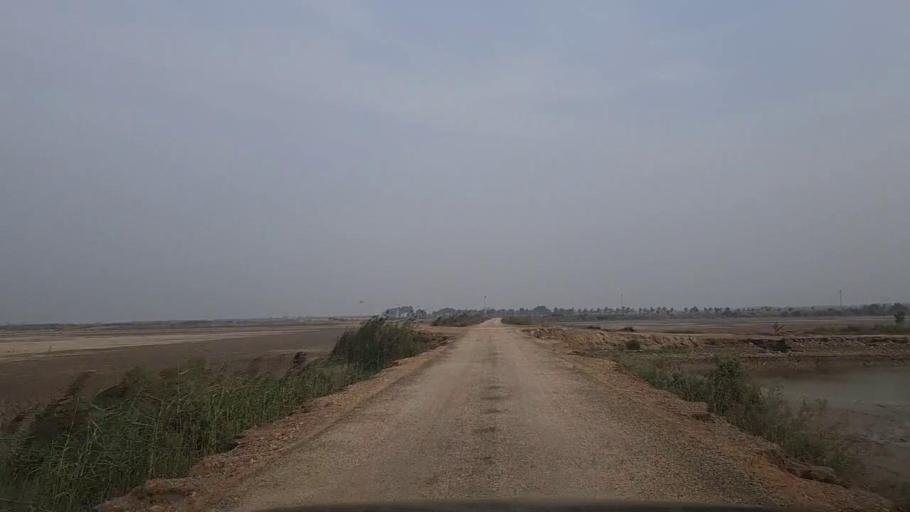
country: PK
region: Sindh
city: Chuhar Jamali
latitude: 24.5030
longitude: 67.8783
